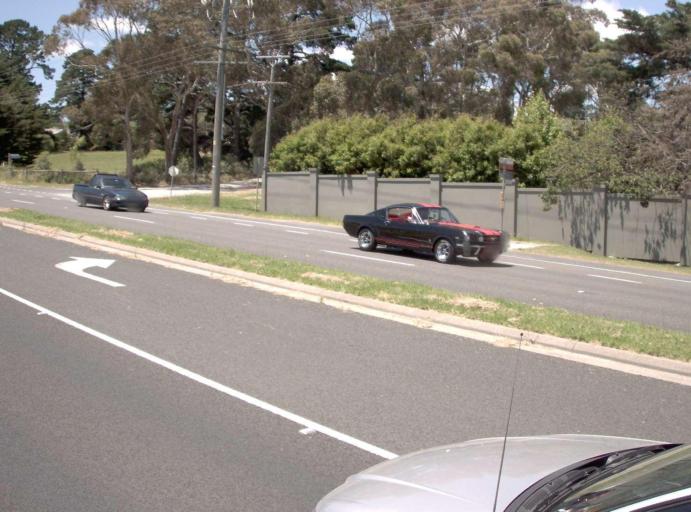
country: AU
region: Victoria
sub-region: Mornington Peninsula
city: Mornington
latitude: -38.2116
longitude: 145.0677
